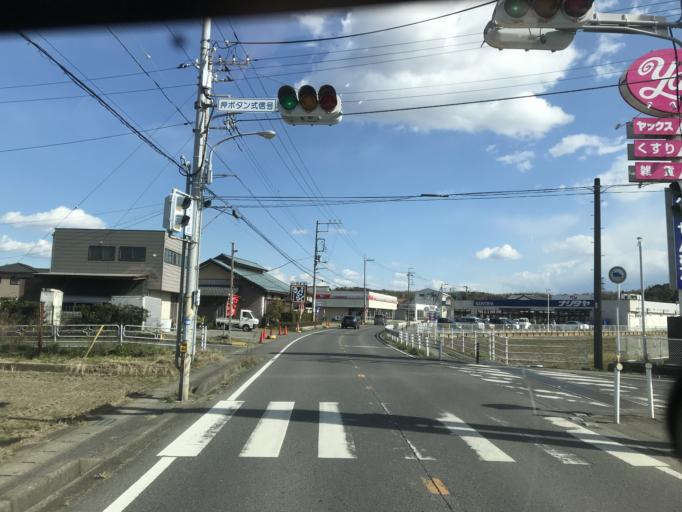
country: JP
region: Chiba
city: Katori-shi
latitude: 35.8988
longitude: 140.4092
